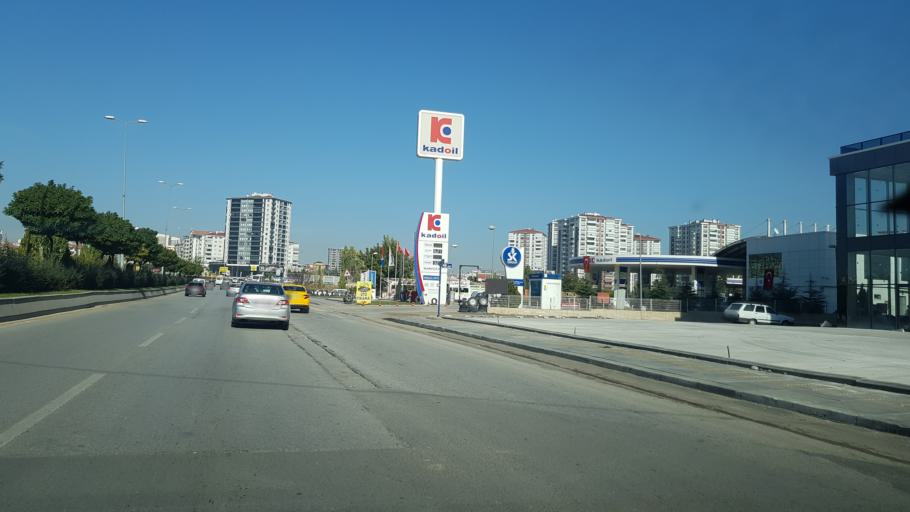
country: TR
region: Ankara
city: Etimesgut
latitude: 39.9676
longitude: 32.6078
